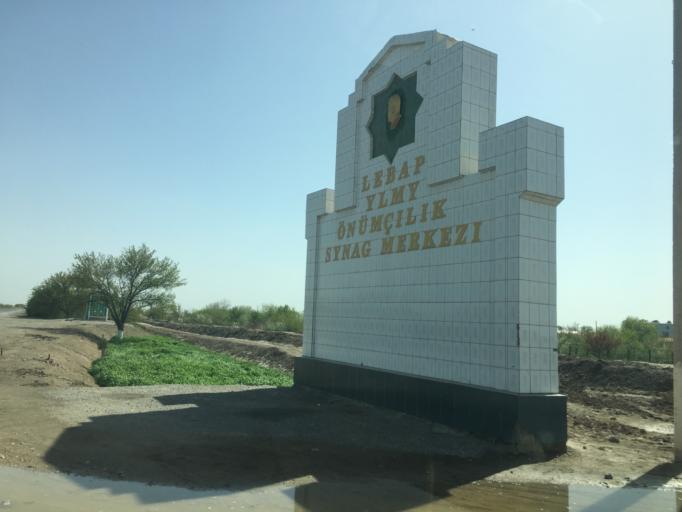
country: TM
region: Lebap
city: Turkmenabat
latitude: 38.9684
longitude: 63.6549
